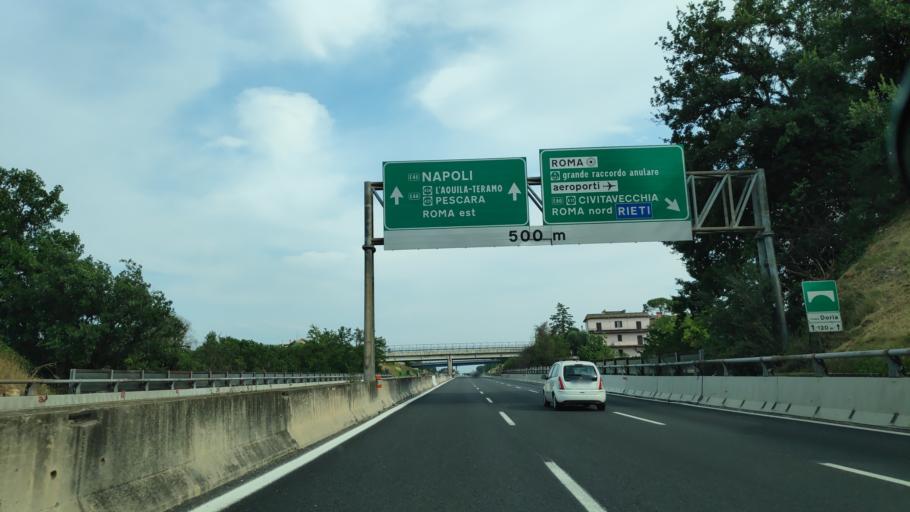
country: IT
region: Latium
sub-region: Citta metropolitana di Roma Capitale
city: Fiano Romano
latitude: 42.1765
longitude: 12.6052
